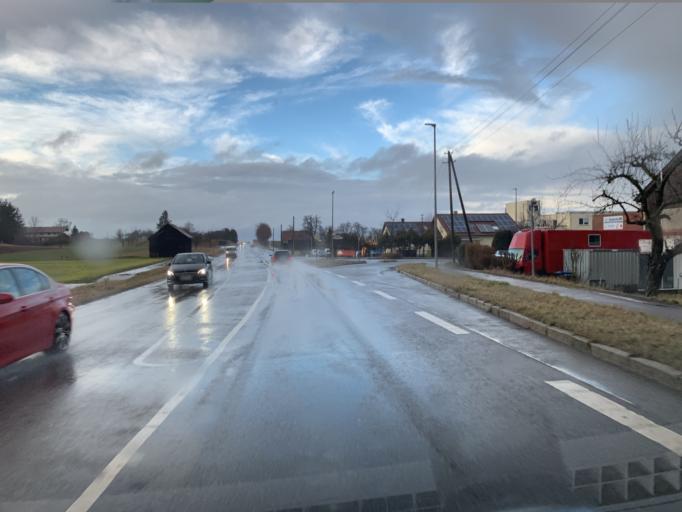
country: DE
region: Baden-Wuerttemberg
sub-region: Regierungsbezirk Stuttgart
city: Magstadt
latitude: 48.7278
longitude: 8.9635
